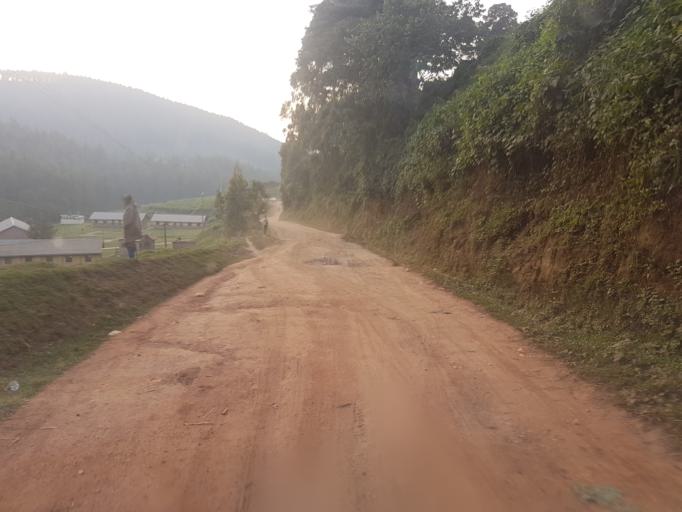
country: UG
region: Western Region
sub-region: Kanungu District
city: Kanungu
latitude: -0.9844
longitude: 29.8484
